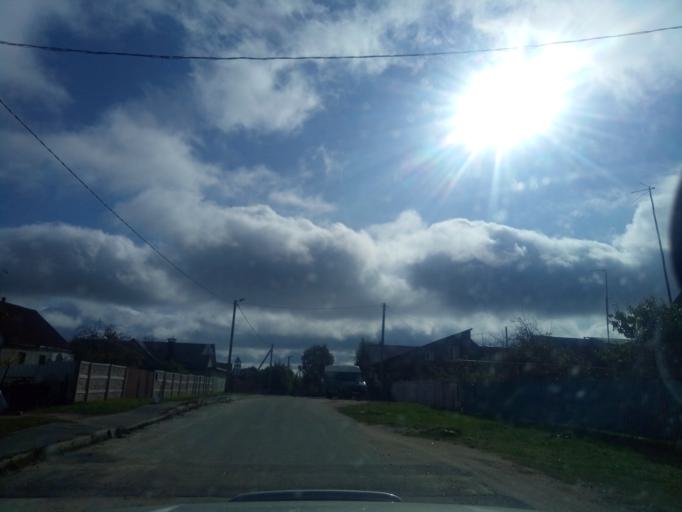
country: BY
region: Minsk
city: Zaslawye
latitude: 54.0161
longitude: 27.2902
